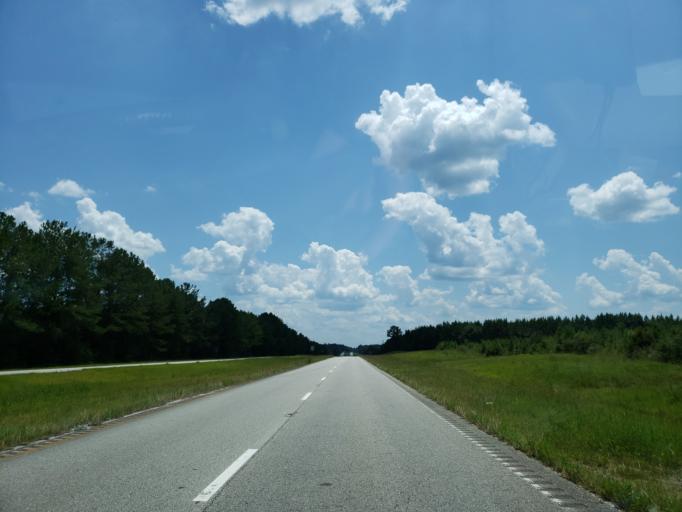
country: US
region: Mississippi
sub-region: Wayne County
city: Belmont
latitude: 31.3887
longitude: -88.4793
